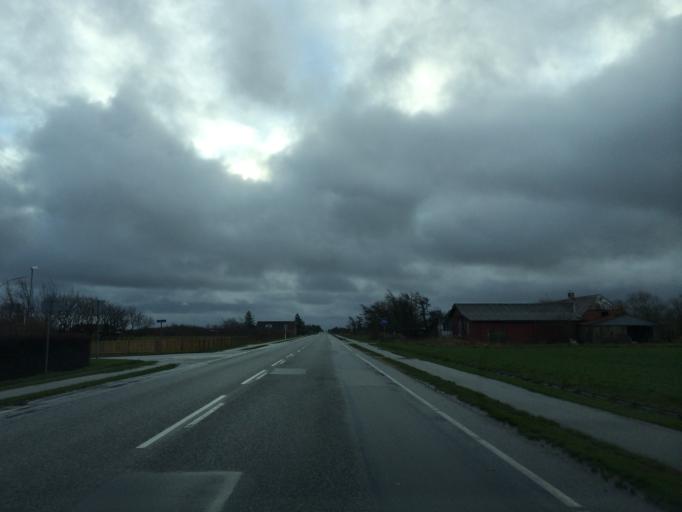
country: DK
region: Central Jutland
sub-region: Ringkobing-Skjern Kommune
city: Ringkobing
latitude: 56.1430
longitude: 8.2824
